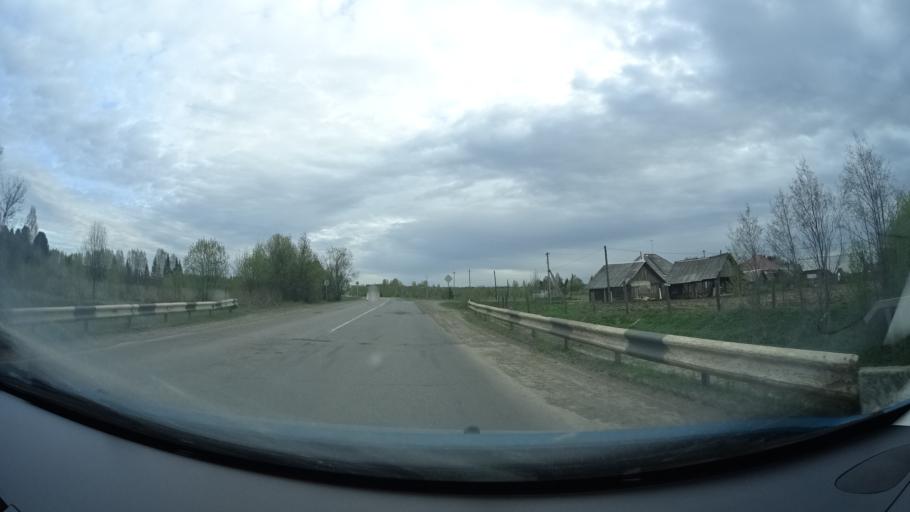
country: RU
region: Perm
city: Osa
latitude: 57.3680
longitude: 55.6062
